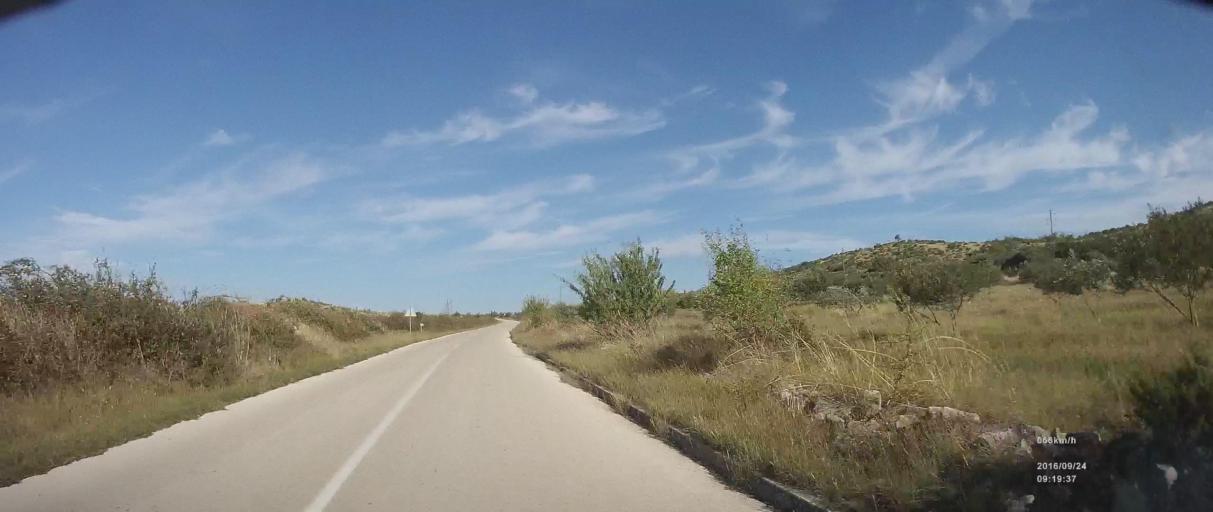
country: HR
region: Zadarska
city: Polaca
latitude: 44.0632
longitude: 15.5032
